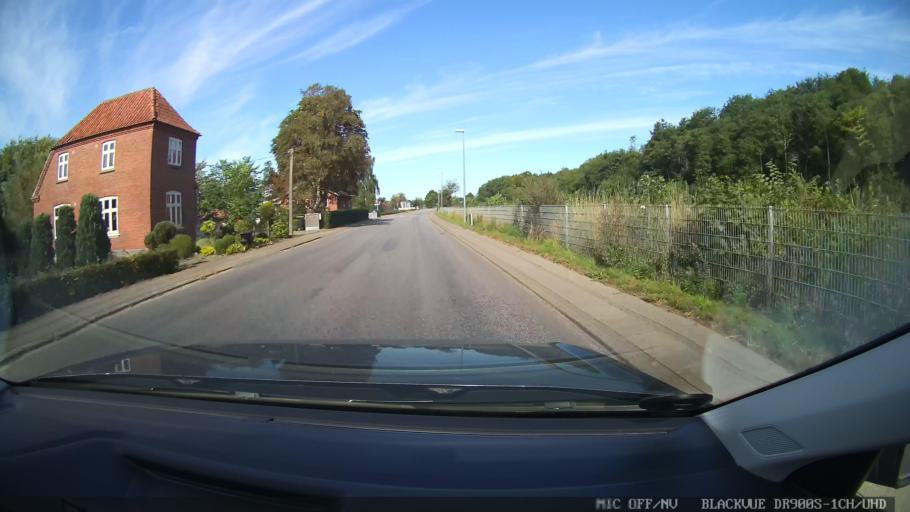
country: DK
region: North Denmark
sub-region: Mariagerfjord Kommune
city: Hobro
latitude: 56.5444
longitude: 9.8478
